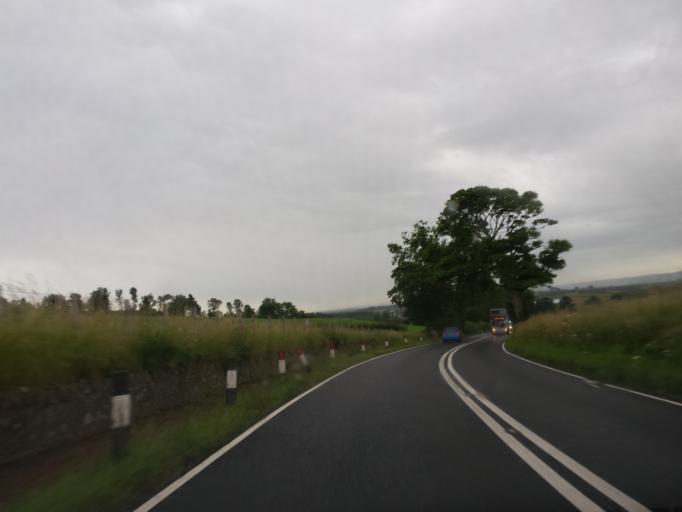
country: GB
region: Scotland
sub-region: Fife
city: Newport-On-Tay
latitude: 56.4261
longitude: -2.9251
